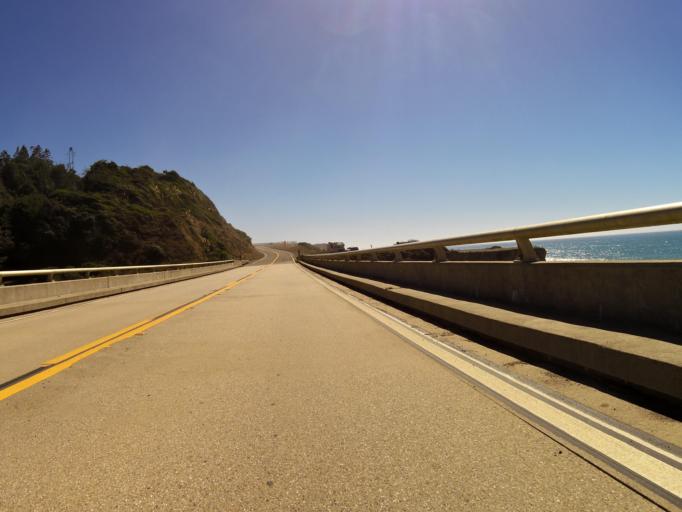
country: US
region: California
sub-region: Mendocino County
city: Fort Bragg
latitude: 39.7031
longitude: -123.8037
